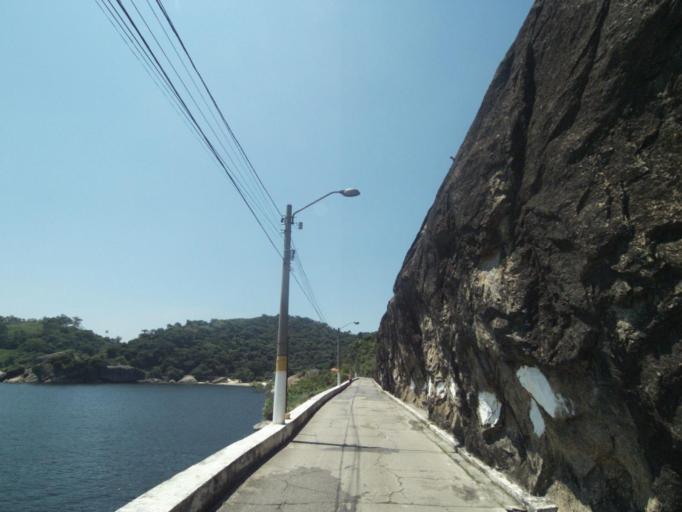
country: BR
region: Rio de Janeiro
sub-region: Niteroi
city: Niteroi
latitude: -22.9312
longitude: -43.1252
